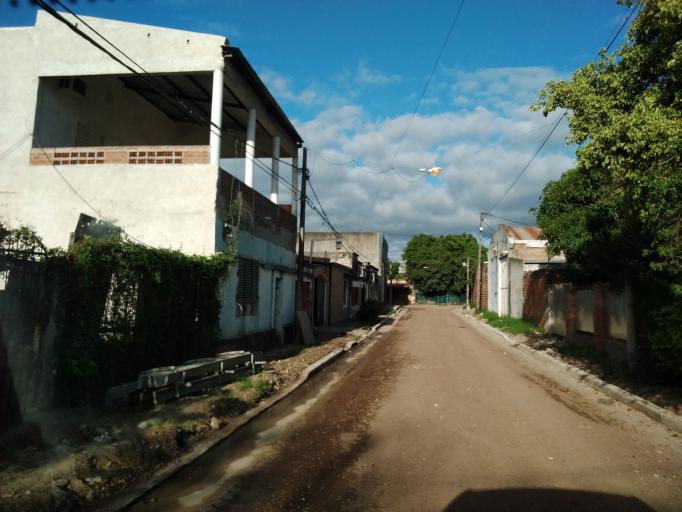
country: AR
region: Corrientes
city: Corrientes
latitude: -27.4785
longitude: -58.8092
